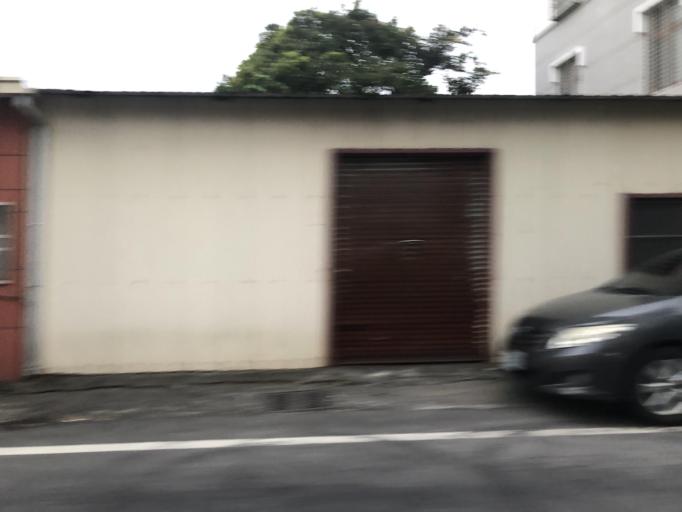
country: TW
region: Taiwan
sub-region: Tainan
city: Tainan
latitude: 23.0213
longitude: 120.2847
